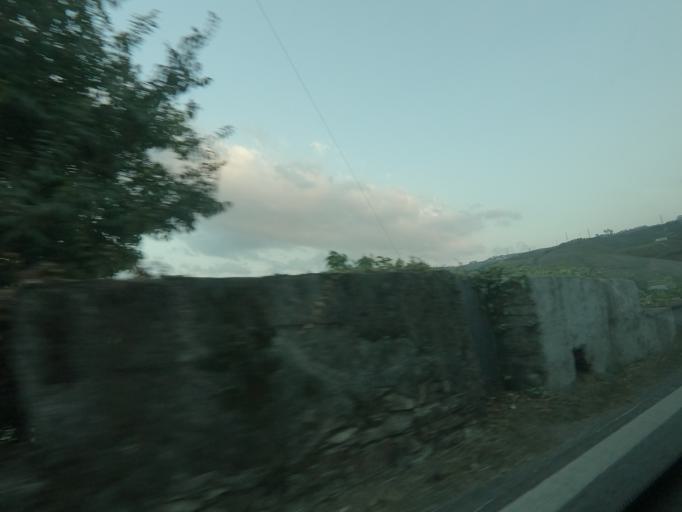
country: PT
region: Vila Real
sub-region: Peso da Regua
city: Godim
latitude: 41.1519
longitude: -7.8091
